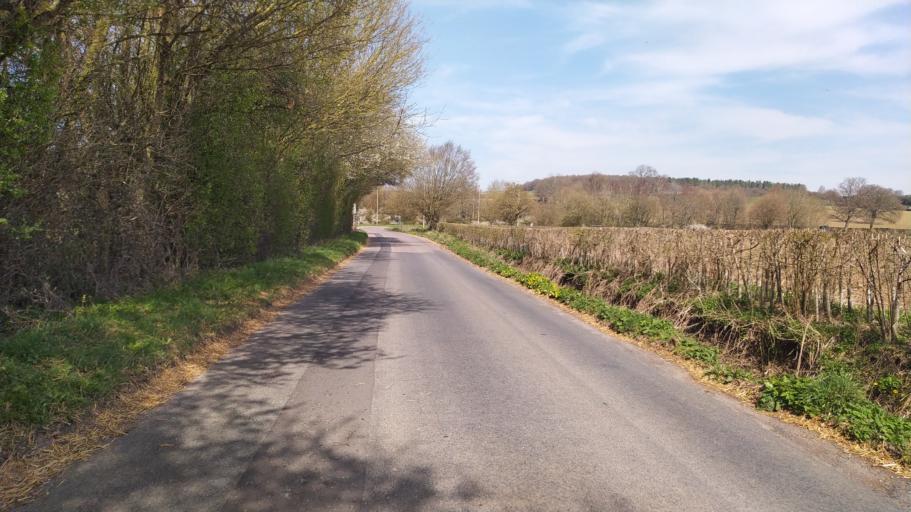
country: GB
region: England
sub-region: Hampshire
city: Four Marks
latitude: 51.0797
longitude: -1.1156
